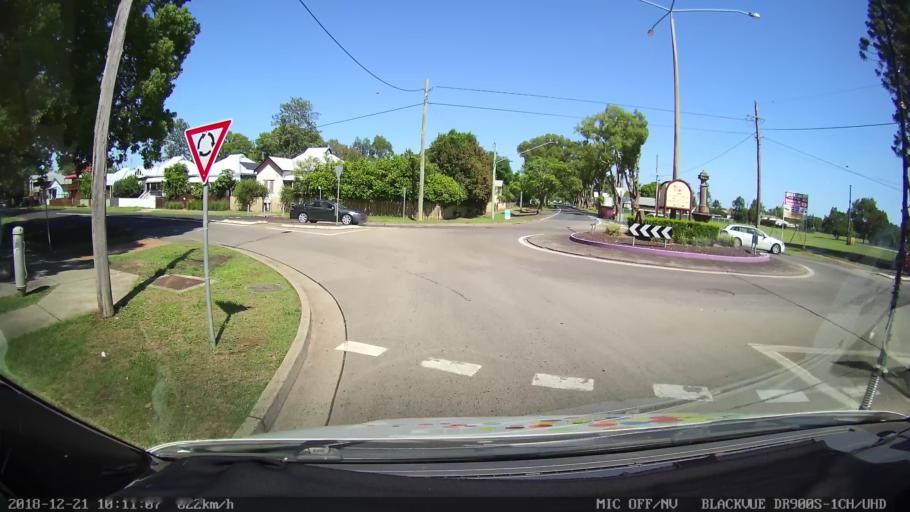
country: AU
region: New South Wales
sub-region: Clarence Valley
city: South Grafton
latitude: -29.7055
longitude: 152.9339
